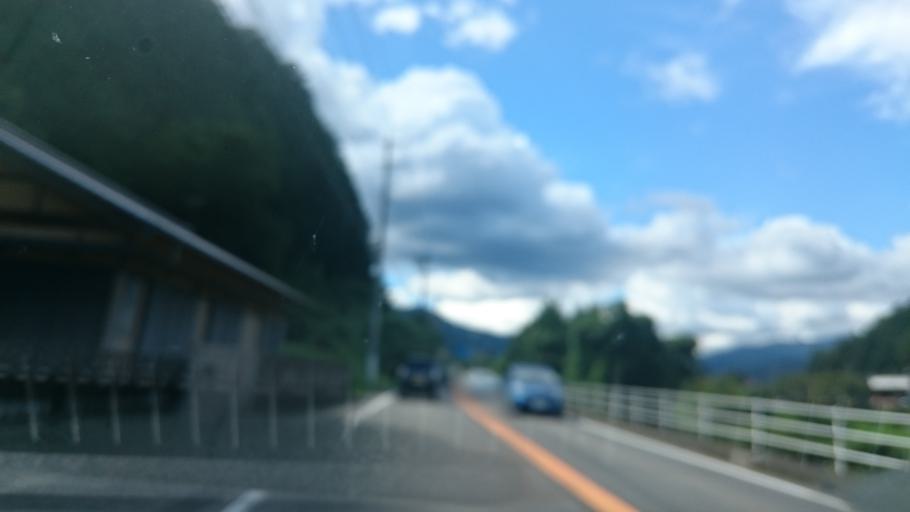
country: JP
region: Gifu
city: Nakatsugawa
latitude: 35.6329
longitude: 137.4491
